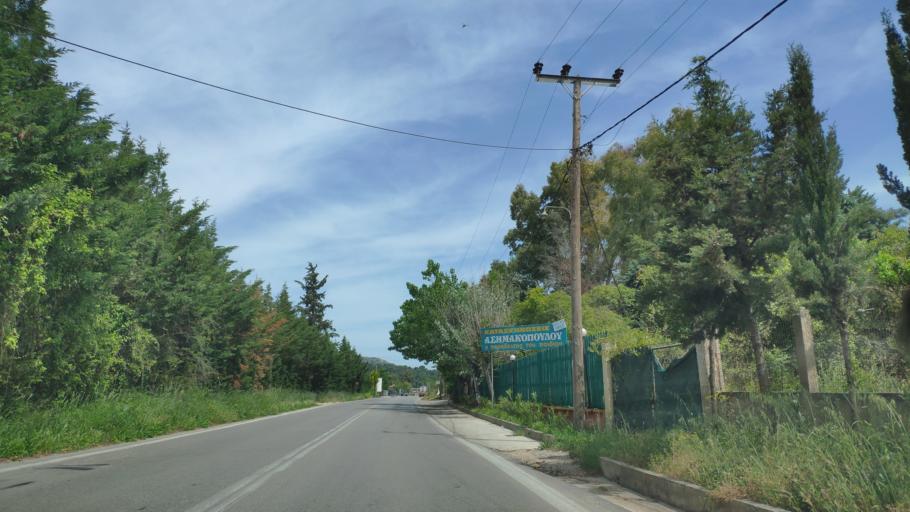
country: GR
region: Attica
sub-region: Nomarchia Anatolikis Attikis
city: Afidnes
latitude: 38.1903
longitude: 23.8544
